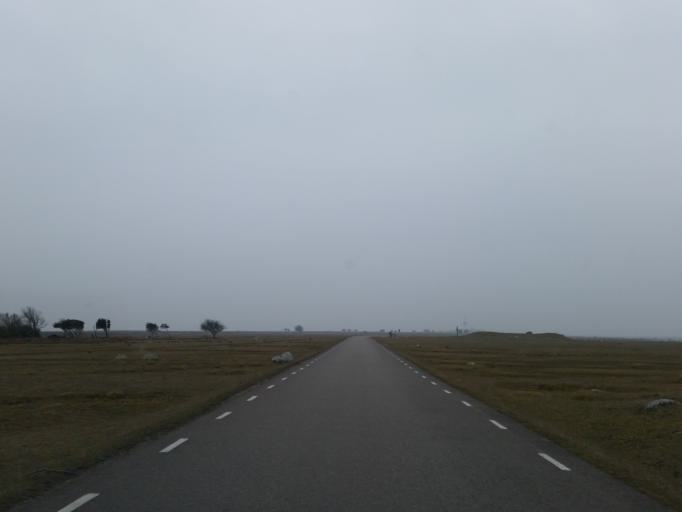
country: SE
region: Kalmar
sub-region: Morbylanga Kommun
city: Moerbylanga
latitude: 56.2114
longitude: 16.4068
